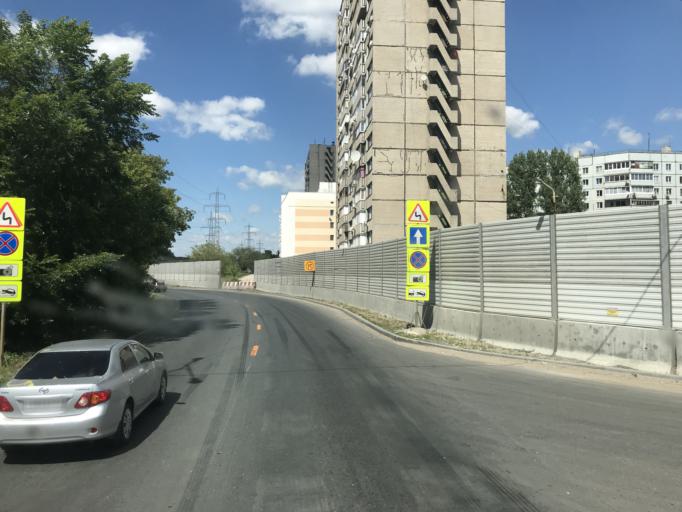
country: RU
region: Samara
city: Zhigulevsk
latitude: 53.4709
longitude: 49.5128
